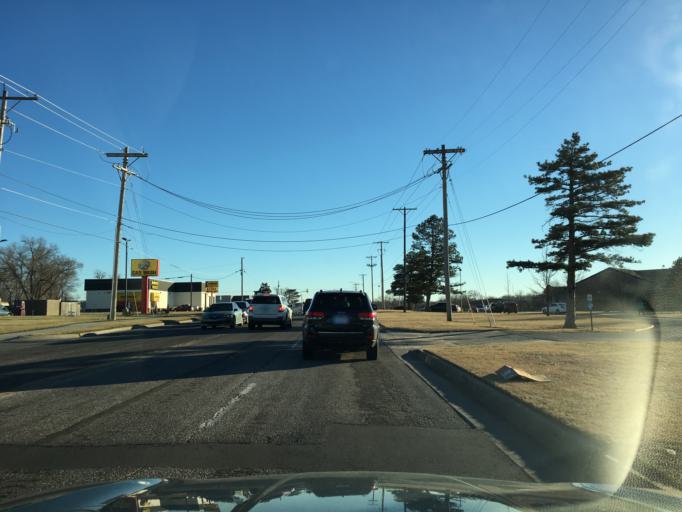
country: US
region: Kansas
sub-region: Sedgwick County
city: Bellaire
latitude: 37.6985
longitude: -97.2263
